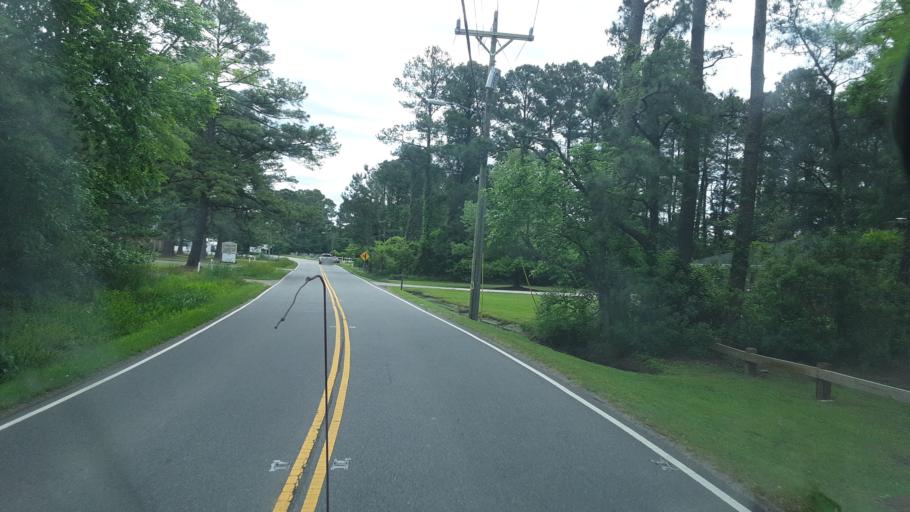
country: US
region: Virginia
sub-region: City of Virginia Beach
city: Virginia Beach
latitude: 36.7313
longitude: -75.9842
